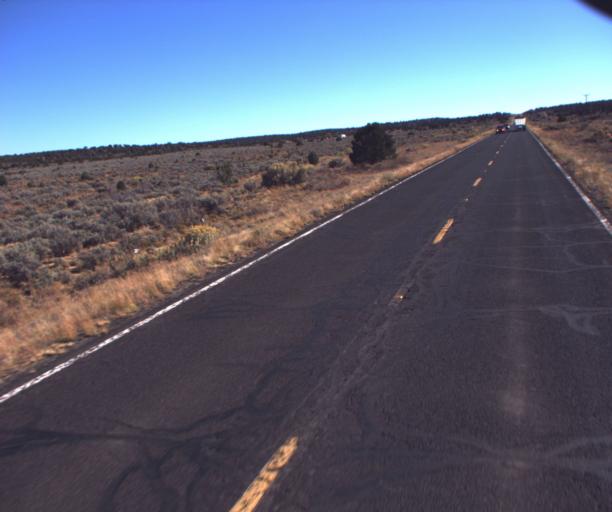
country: US
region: Arizona
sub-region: Apache County
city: Ganado
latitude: 35.6023
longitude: -109.5398
